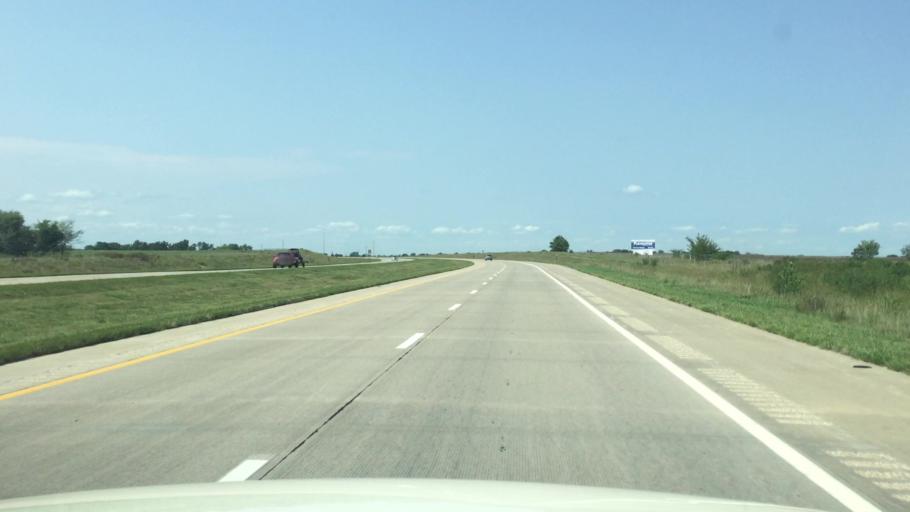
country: US
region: Kansas
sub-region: Linn County
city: Pleasanton
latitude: 38.1704
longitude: -94.6958
